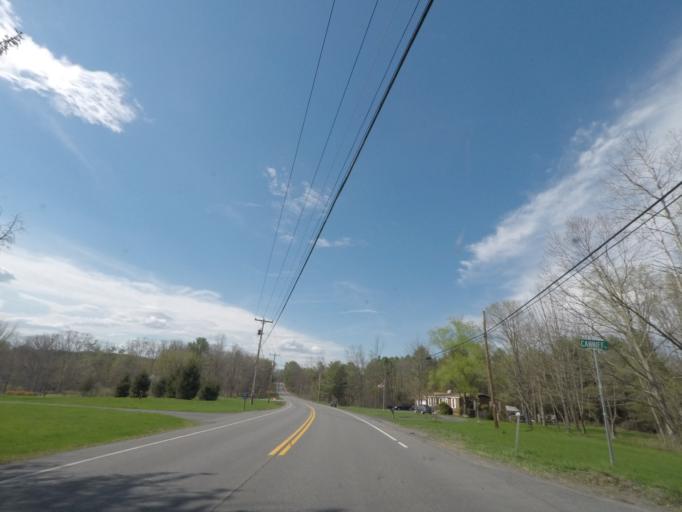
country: US
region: New York
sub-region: Greene County
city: Cairo
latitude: 42.3284
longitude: -74.0158
